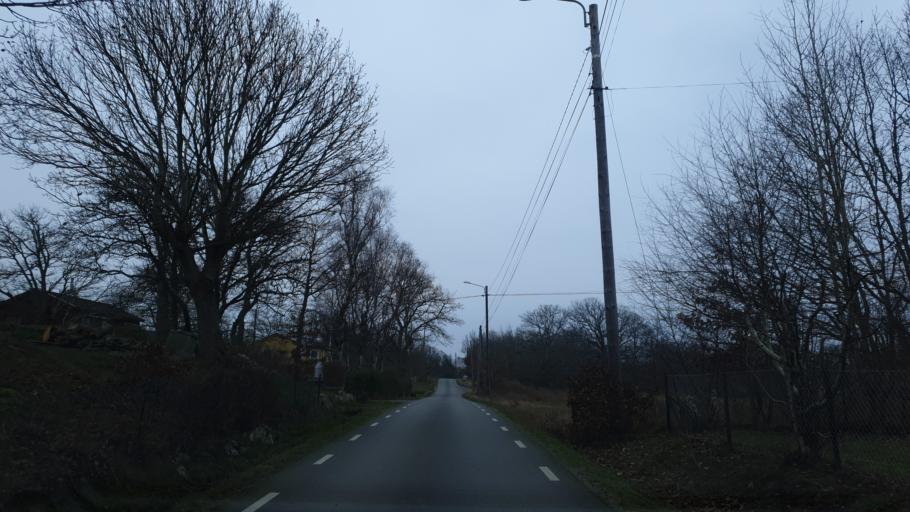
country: SE
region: Blekinge
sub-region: Karlskrona Kommun
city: Karlskrona
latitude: 56.1290
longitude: 15.6196
